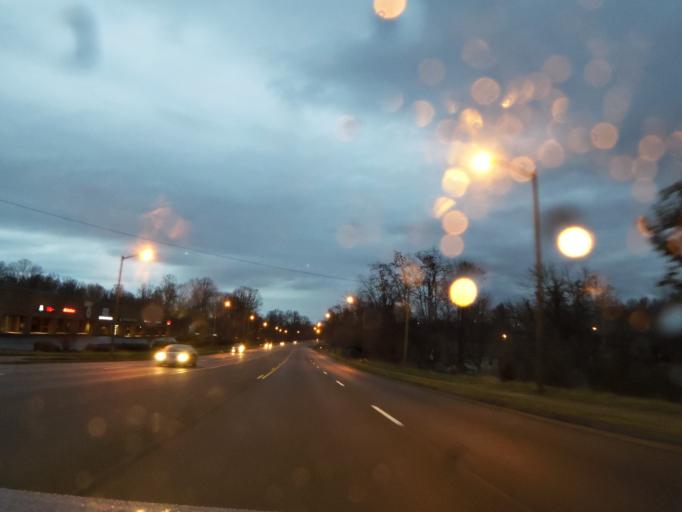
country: US
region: Tennessee
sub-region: Washington County
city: Johnson City
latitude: 36.3164
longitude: -82.3904
